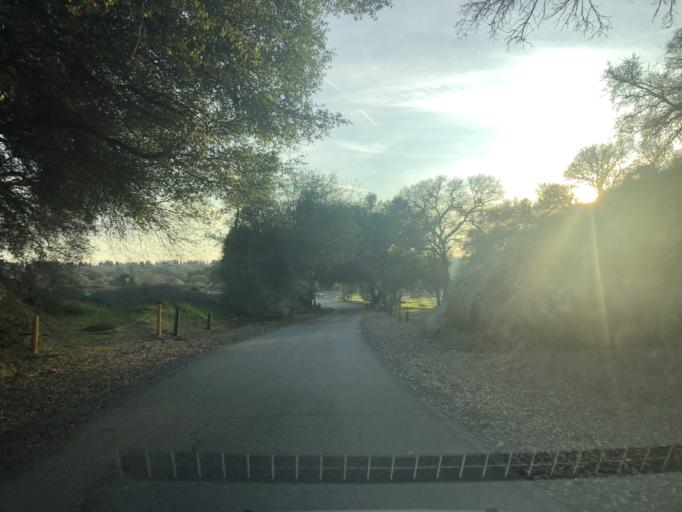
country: US
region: California
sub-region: Sacramento County
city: Gold River
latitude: 38.6394
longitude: -121.2358
